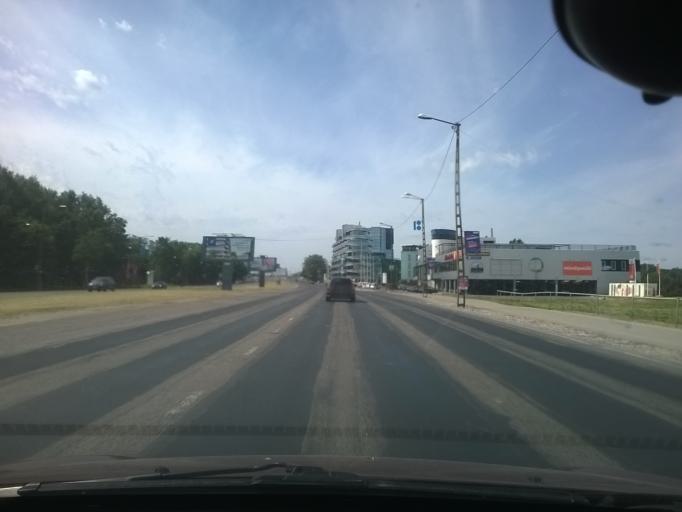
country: EE
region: Harju
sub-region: Tallinna linn
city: Tallinn
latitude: 59.4277
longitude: 24.6675
